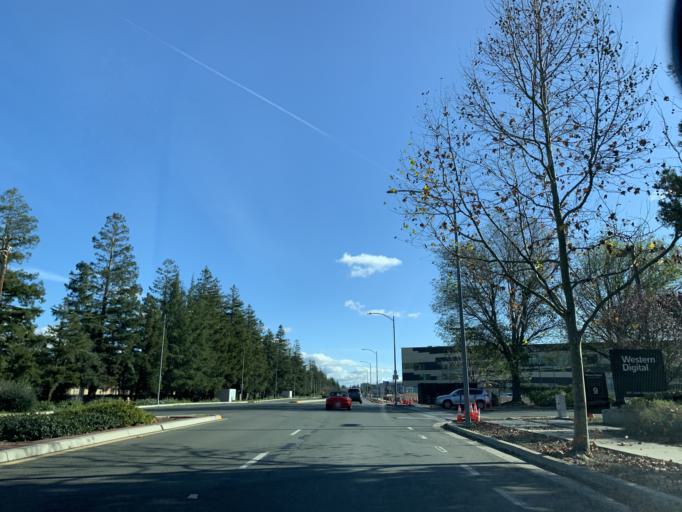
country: US
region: California
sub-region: Santa Clara County
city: Seven Trees
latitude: 37.2472
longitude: -121.7897
